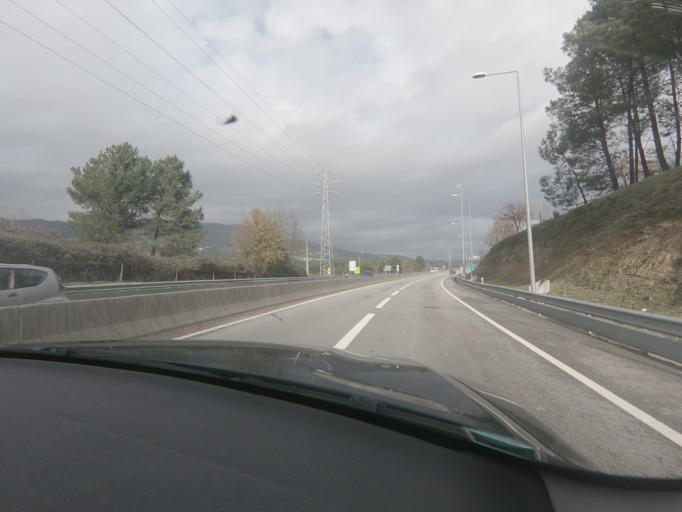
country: PT
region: Vila Real
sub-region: Vila Real
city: Vila Real
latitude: 41.3078
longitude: -7.7506
